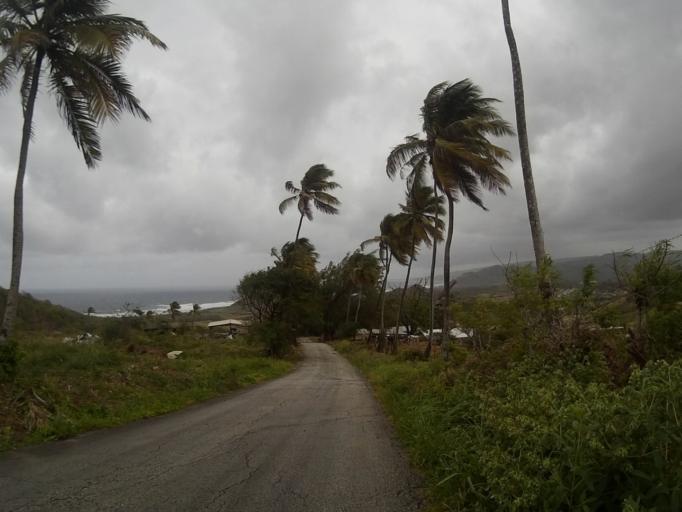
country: BB
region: Saint Andrew
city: Greenland
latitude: 13.2697
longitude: -59.5759
